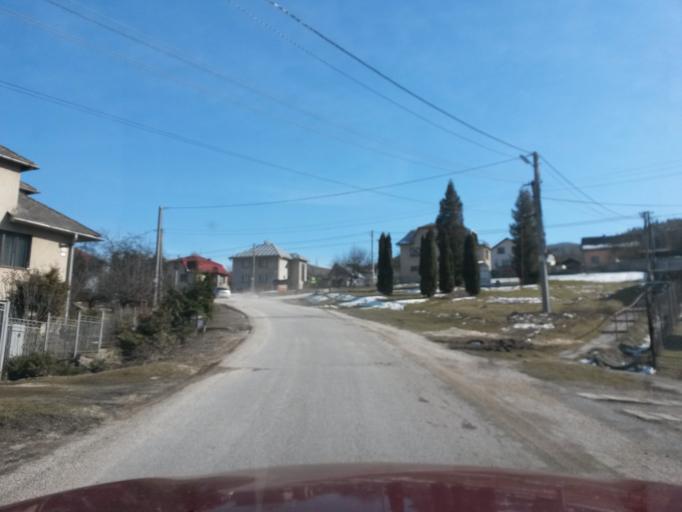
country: SK
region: Kosicky
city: Gelnica
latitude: 48.8714
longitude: 20.9848
